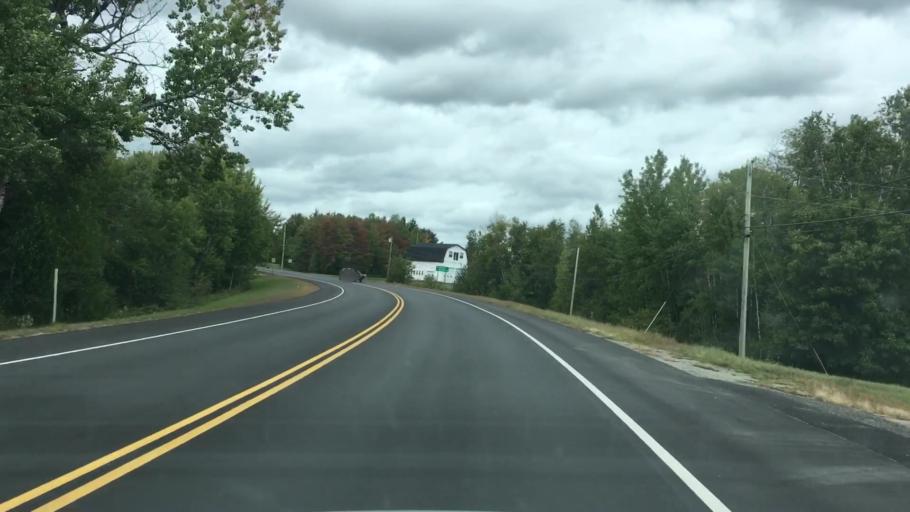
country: US
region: Maine
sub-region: Penobscot County
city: Milford
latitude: 44.9570
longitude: -68.7036
